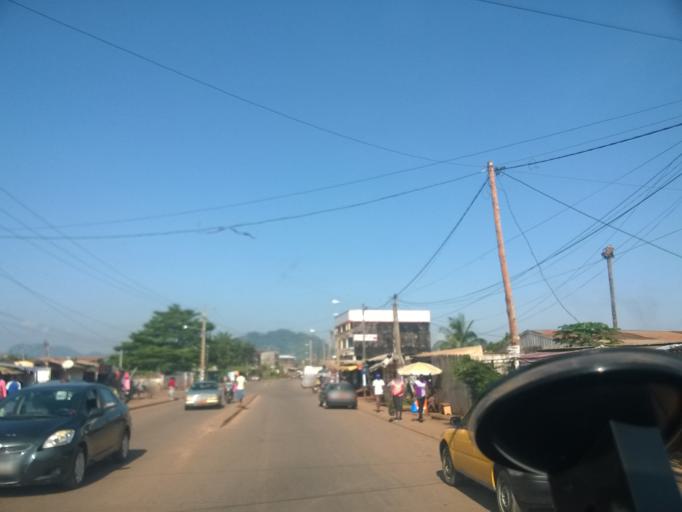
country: CM
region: Centre
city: Yaounde
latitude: 3.8453
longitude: 11.4996
